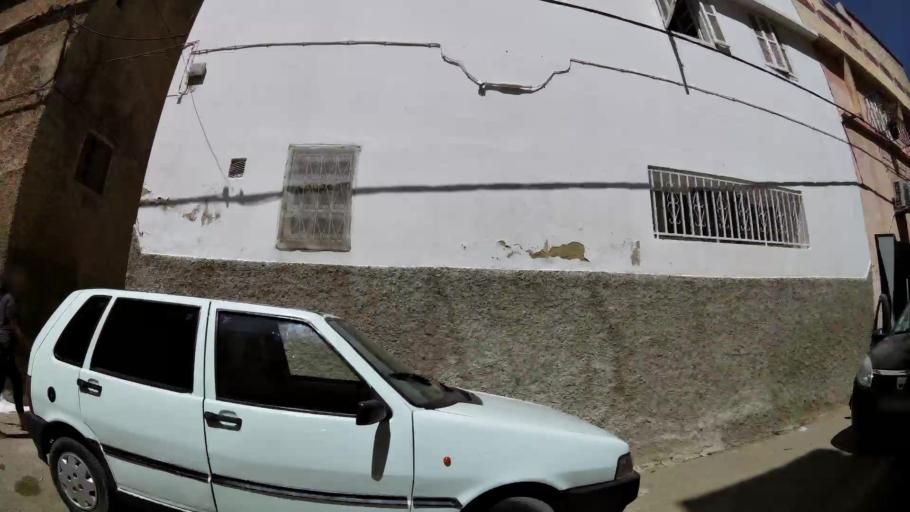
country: MA
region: Meknes-Tafilalet
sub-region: Meknes
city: Meknes
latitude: 33.8704
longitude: -5.5624
